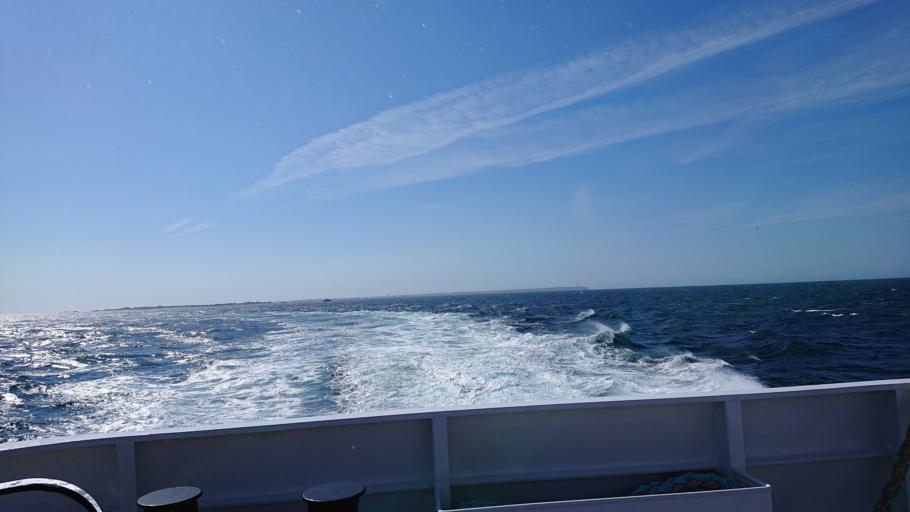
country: FR
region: Brittany
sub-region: Departement du Finistere
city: Le Conquet
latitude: 48.4151
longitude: -4.9415
